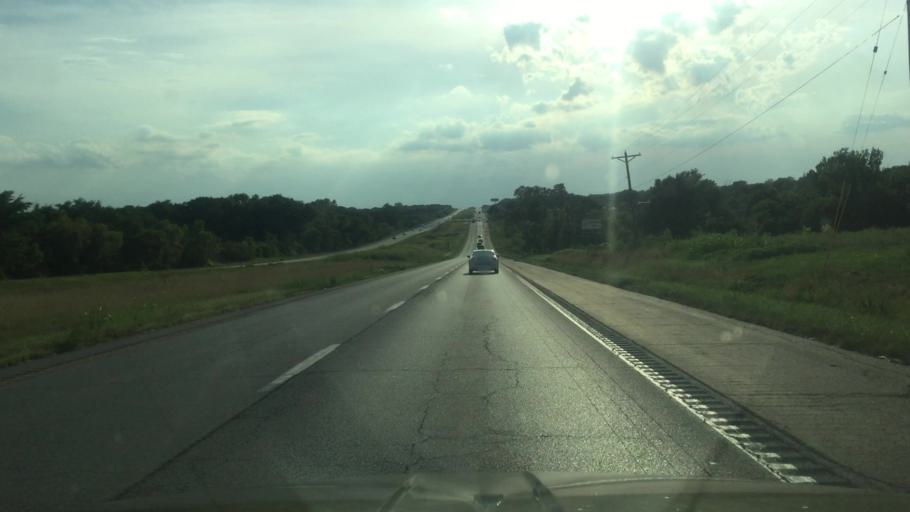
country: US
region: Missouri
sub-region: Jackson County
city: Lone Jack
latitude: 38.8701
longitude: -94.1223
